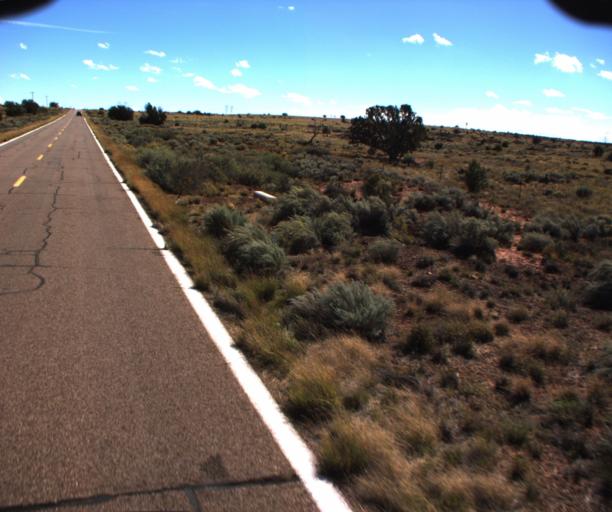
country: US
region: Arizona
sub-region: Apache County
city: Saint Johns
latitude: 34.5740
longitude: -109.6367
